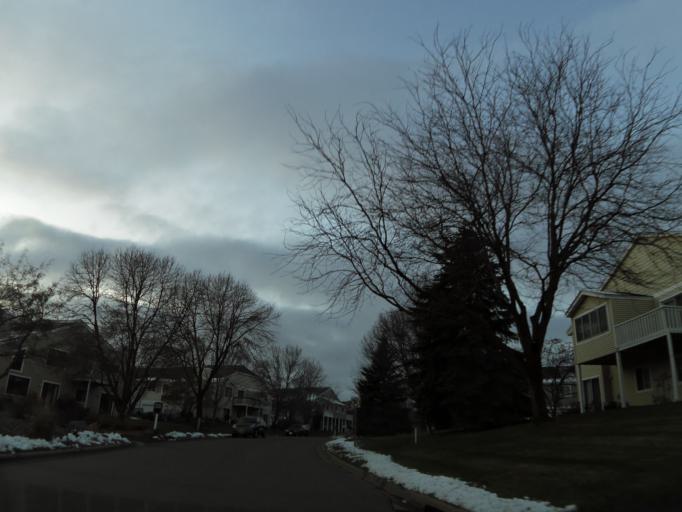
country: US
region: Minnesota
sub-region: Hennepin County
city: Minnetonka Mills
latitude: 44.9013
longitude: -93.4237
